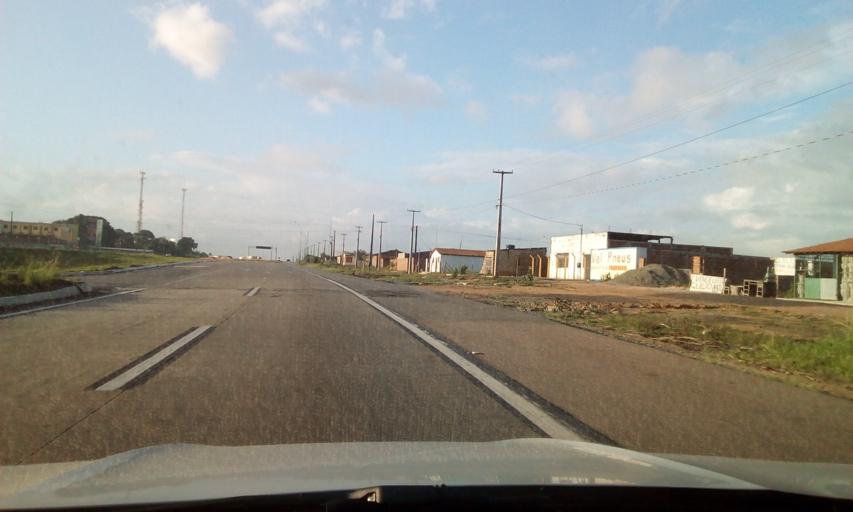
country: BR
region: Pernambuco
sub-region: Goiana
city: Goiana
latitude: -7.4914
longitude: -34.9829
